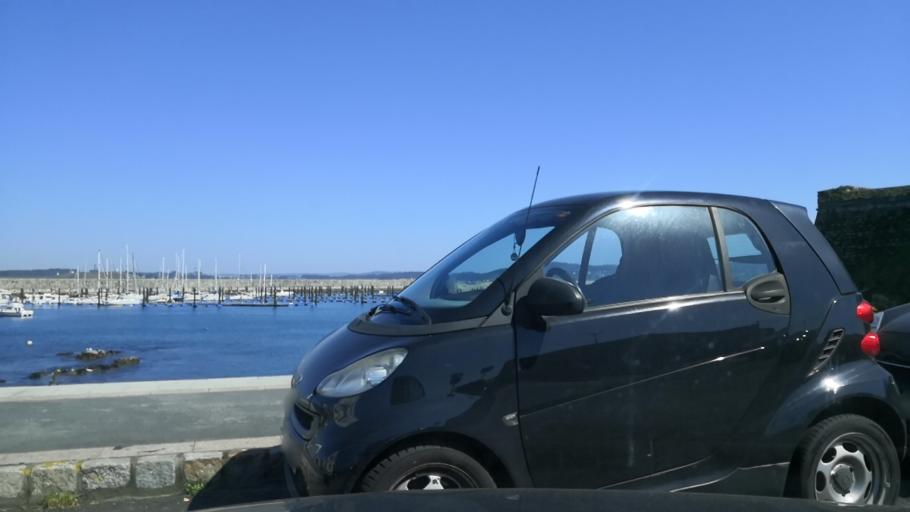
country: ES
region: Galicia
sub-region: Provincia da Coruna
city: A Coruna
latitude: 43.3661
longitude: -8.3886
